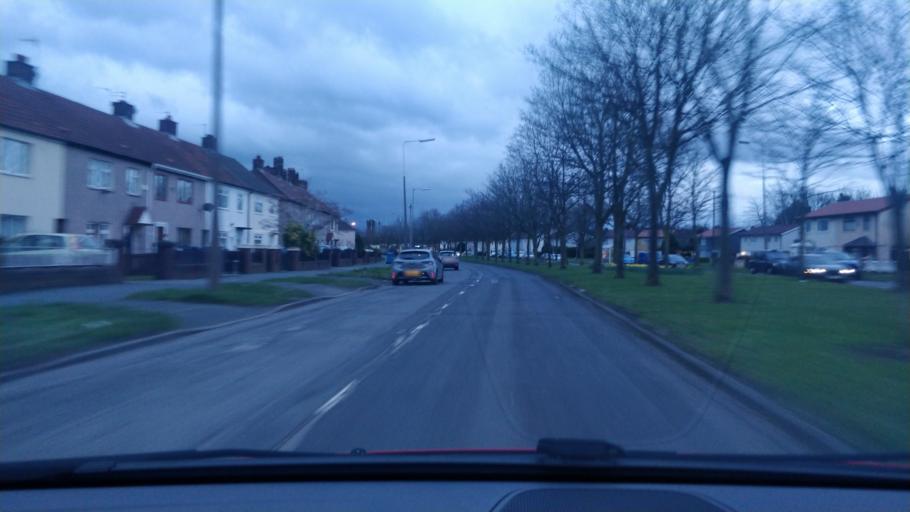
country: GB
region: England
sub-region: Knowsley
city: Knowsley
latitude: 53.4333
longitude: -2.8819
